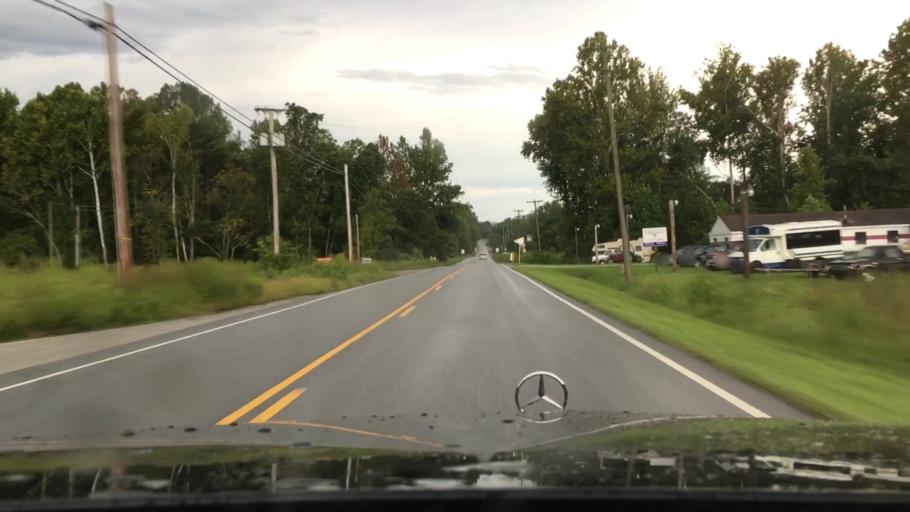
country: US
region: Virginia
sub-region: Amherst County
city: Amherst
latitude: 37.7071
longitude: -79.0240
